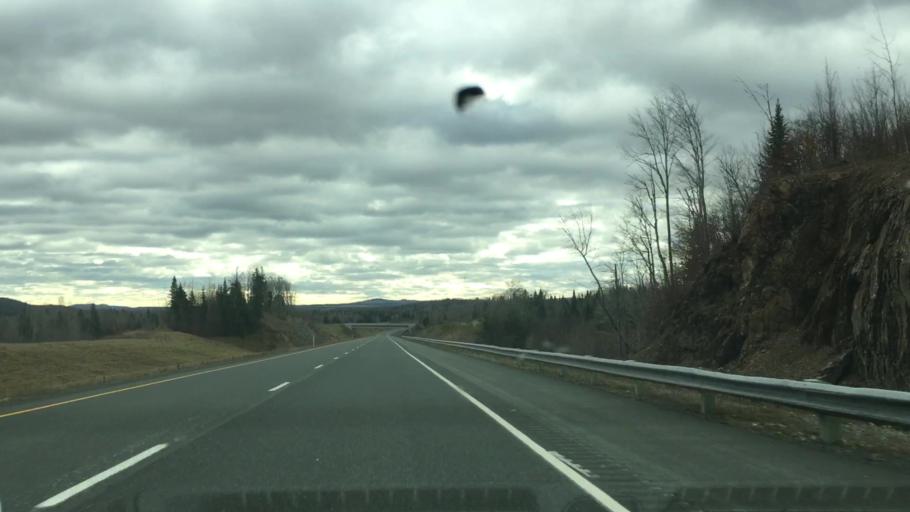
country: US
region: Maine
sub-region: Aroostook County
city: Easton
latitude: 46.6311
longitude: -67.7418
